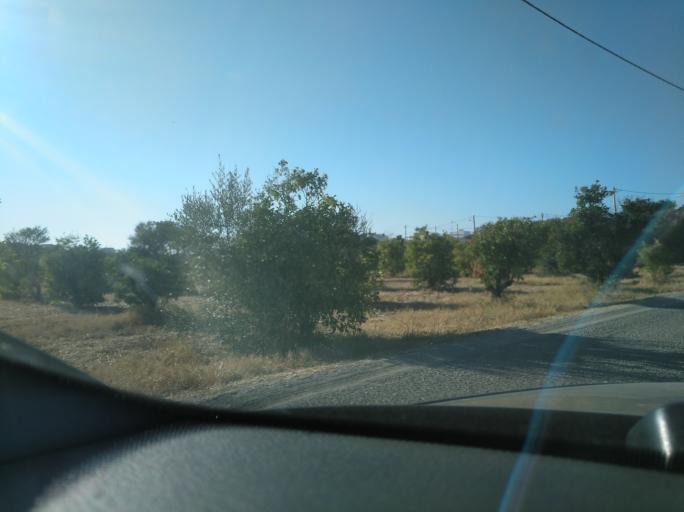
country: PT
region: Faro
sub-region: Vila Real de Santo Antonio
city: Monte Gordo
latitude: 37.1829
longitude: -7.5111
